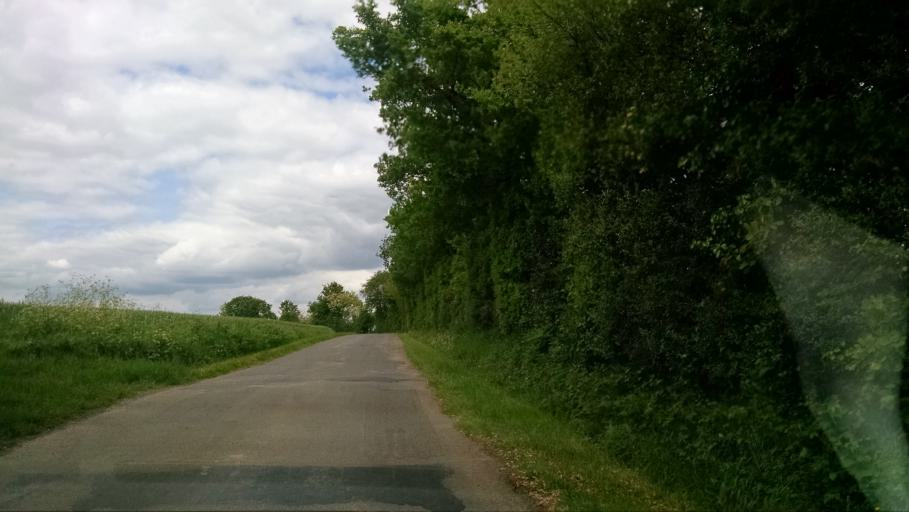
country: FR
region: Pays de la Loire
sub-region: Departement de la Vendee
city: Saint-Hilaire-de-Loulay
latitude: 47.0044
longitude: -1.3727
